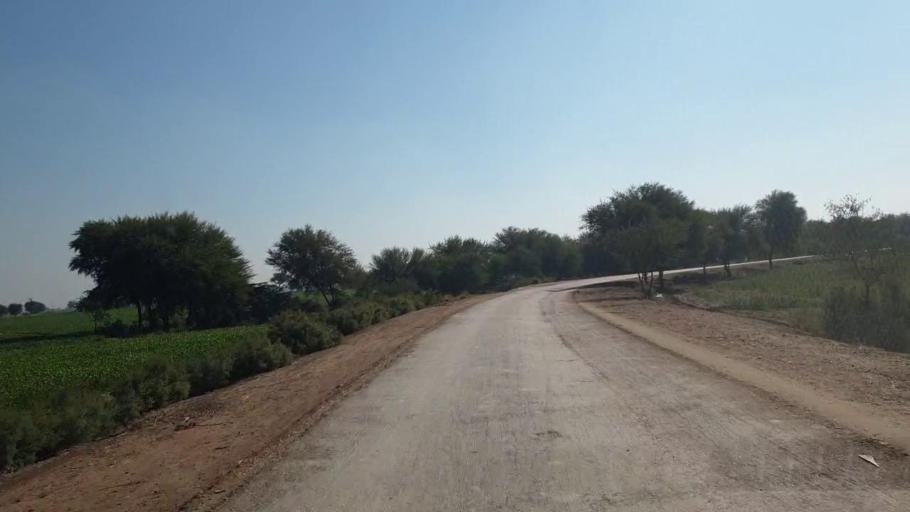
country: PK
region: Sindh
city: Shahpur Chakar
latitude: 26.1191
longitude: 68.6284
